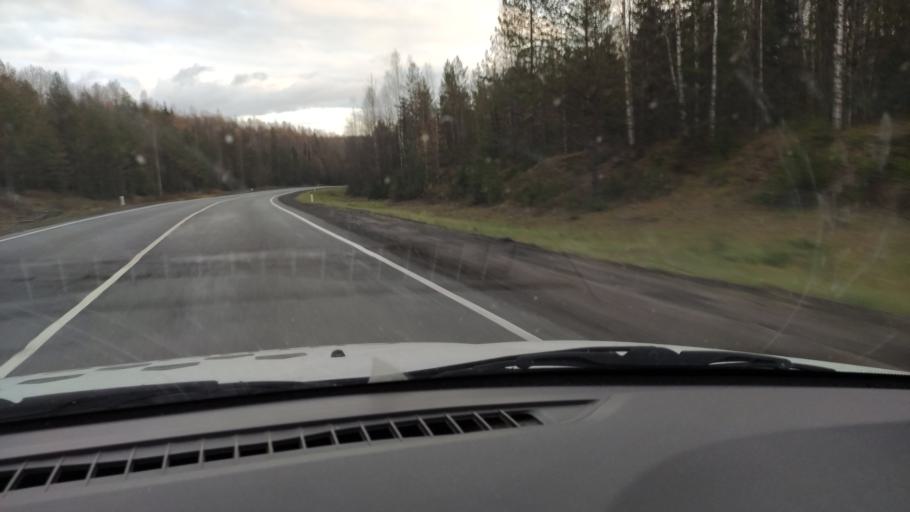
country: RU
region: Kirov
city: Omutninsk
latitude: 58.7506
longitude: 52.0566
